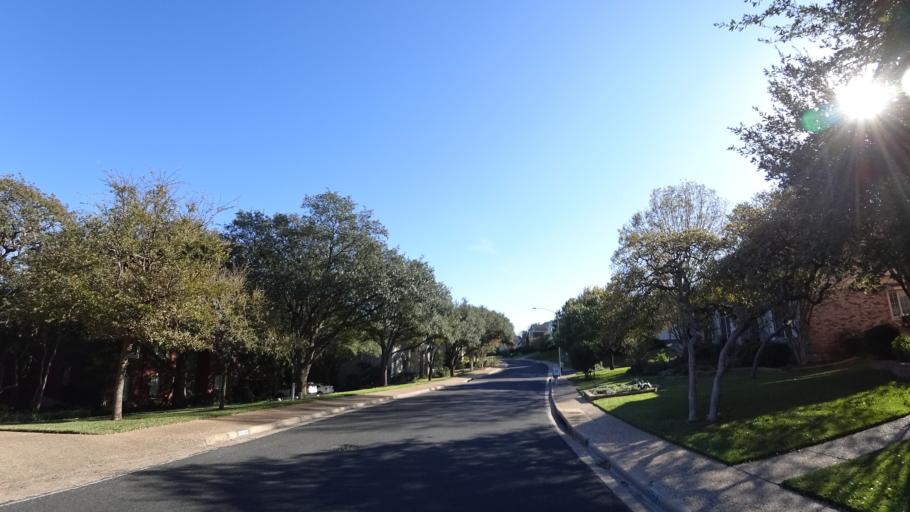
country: US
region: Texas
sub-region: Williamson County
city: Jollyville
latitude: 30.4159
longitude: -97.7755
